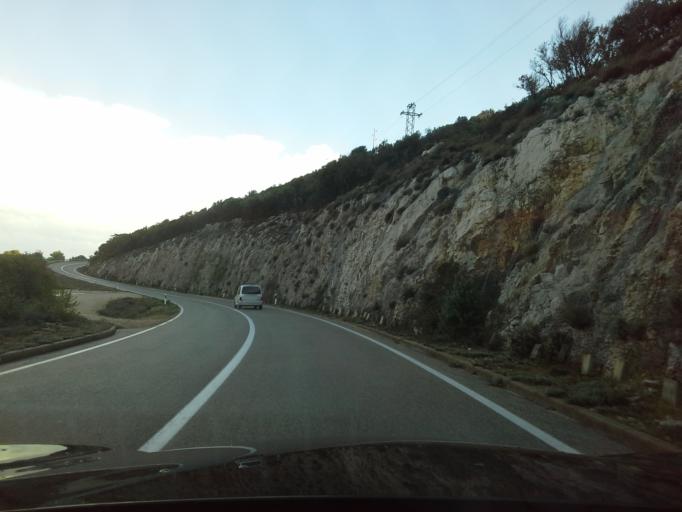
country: HR
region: Primorsko-Goranska
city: Mali Losinj
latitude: 44.6027
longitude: 14.4042
